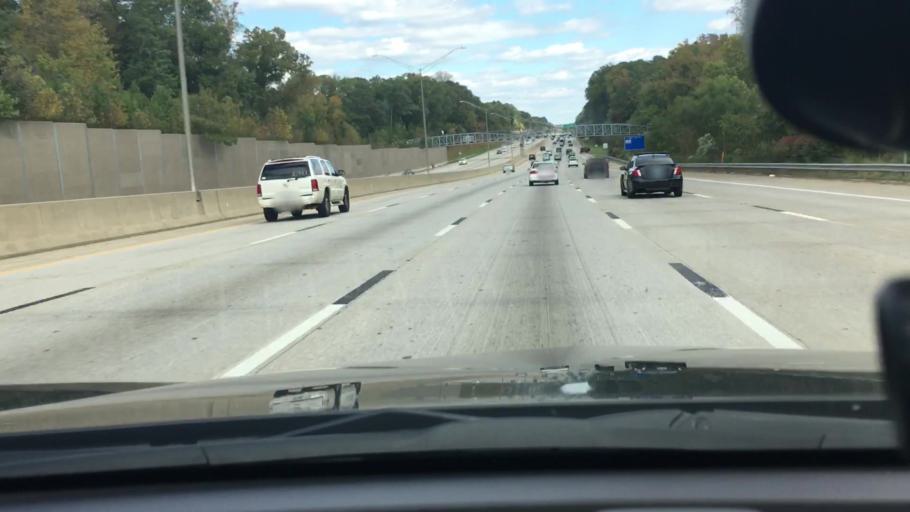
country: US
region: North Carolina
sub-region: Wake County
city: Cary
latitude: 35.7505
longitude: -78.7682
